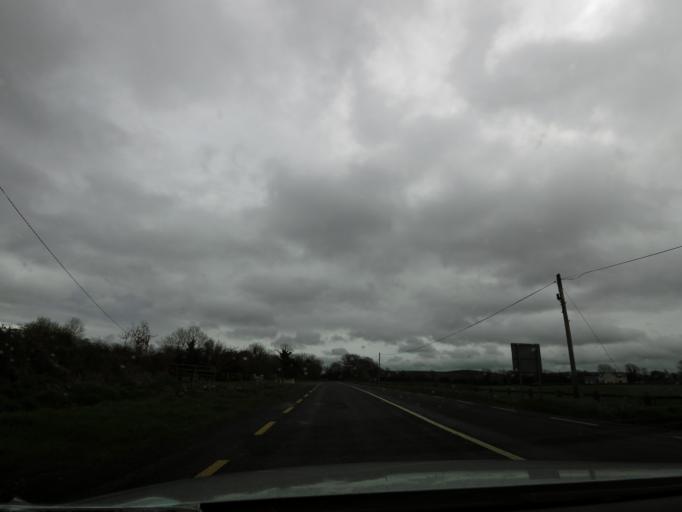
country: IE
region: Leinster
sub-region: Laois
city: Rathdowney
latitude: 52.7194
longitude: -7.5121
